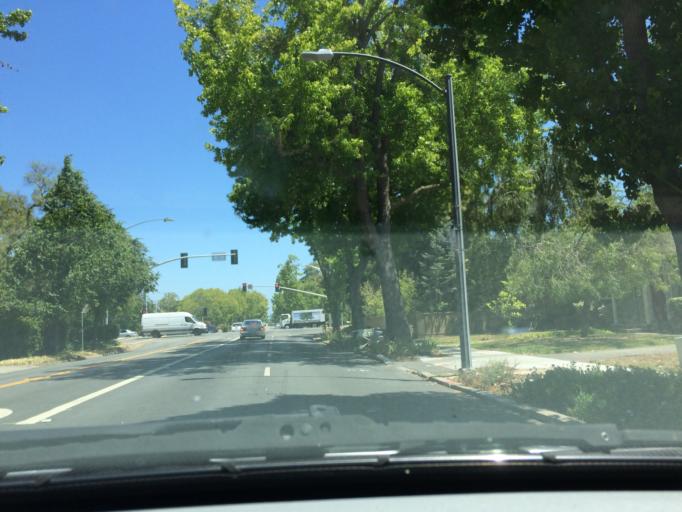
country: US
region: California
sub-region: Santa Clara County
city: Palo Alto
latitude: 37.4362
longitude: -122.1338
